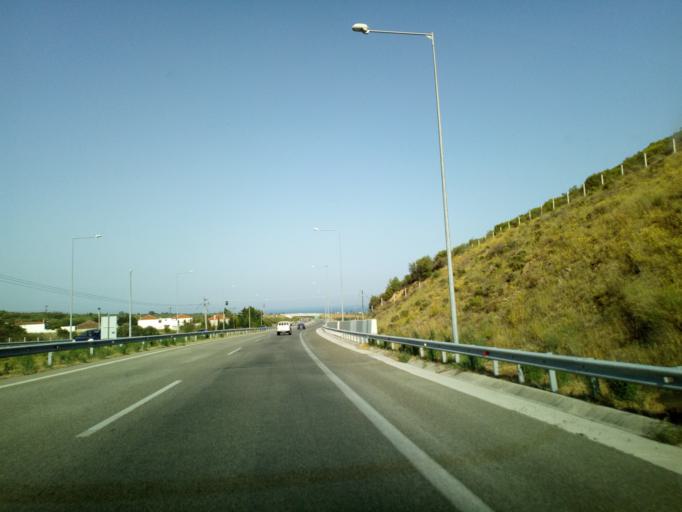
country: GR
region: Central Macedonia
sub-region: Nomos Thessalonikis
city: Nea Vrasna
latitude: 40.7013
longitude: 23.6509
